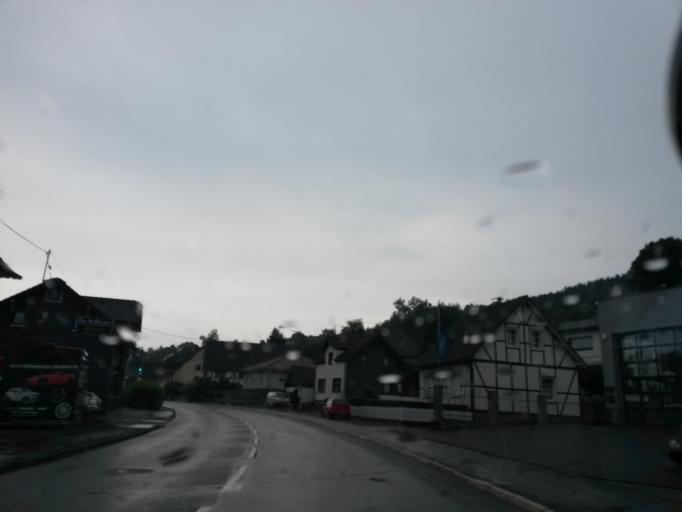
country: DE
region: North Rhine-Westphalia
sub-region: Regierungsbezirk Koln
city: Engelskirchen
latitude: 50.9889
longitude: 7.4743
